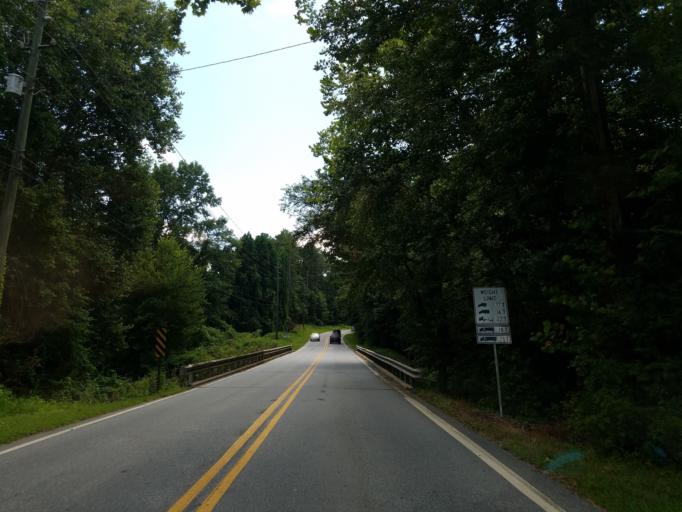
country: US
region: Georgia
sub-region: Fulton County
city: Alpharetta
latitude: 34.0972
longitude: -84.2273
